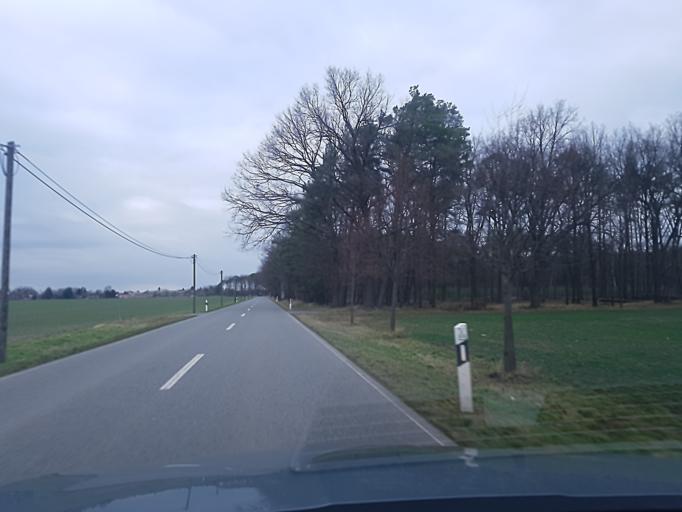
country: DE
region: Brandenburg
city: Sonnewalde
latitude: 51.6801
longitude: 13.6848
